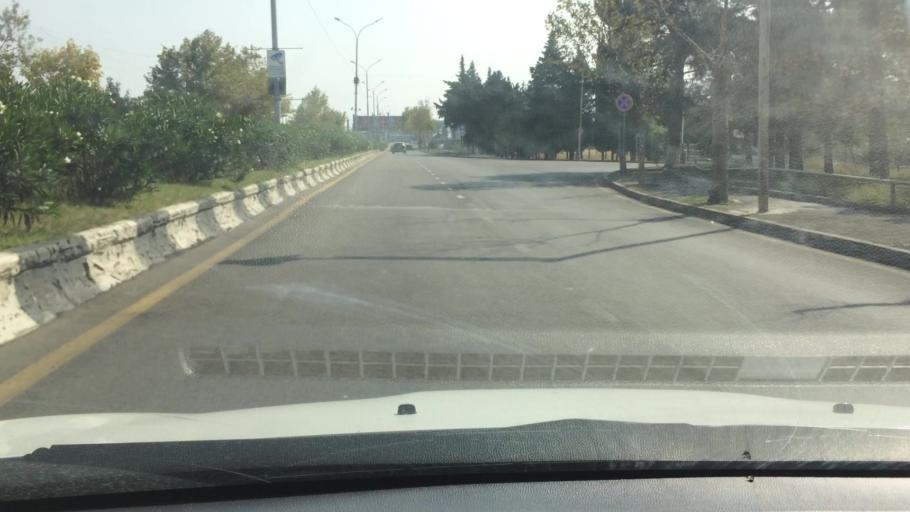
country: GE
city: Didi Lilo
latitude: 41.6764
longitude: 44.9604
